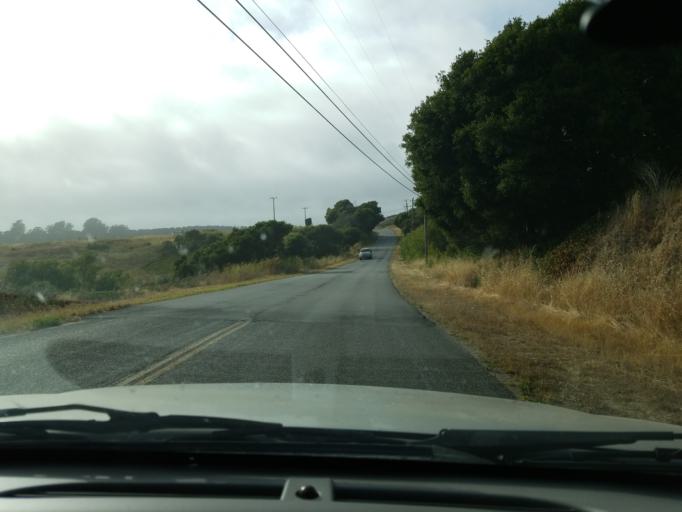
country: US
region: California
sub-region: Monterey County
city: Elkhorn
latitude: 36.8460
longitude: -121.7487
